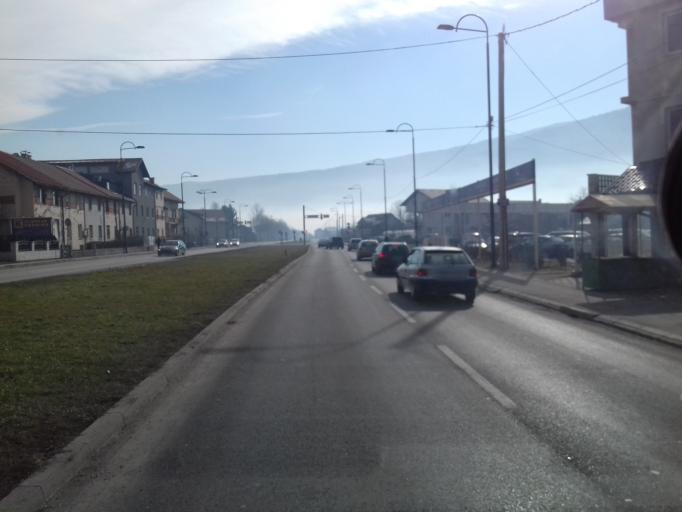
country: BA
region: Federation of Bosnia and Herzegovina
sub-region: Kanton Sarajevo
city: Sarajevo
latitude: 43.8170
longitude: 18.3083
